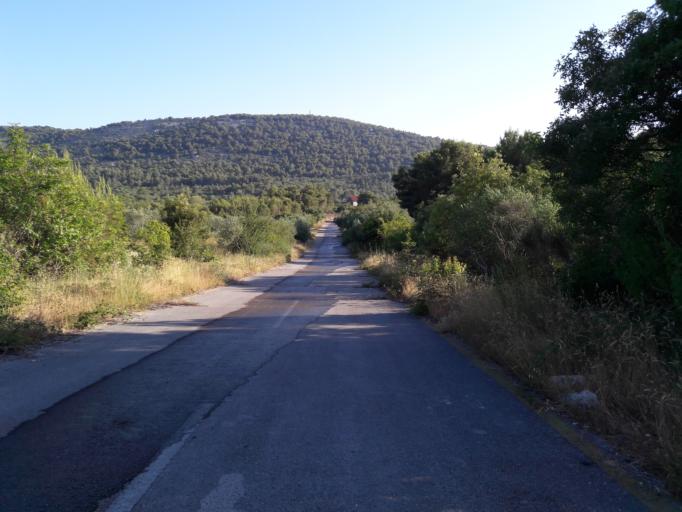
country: HR
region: Sibensko-Kniniska
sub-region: Grad Sibenik
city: Sibenik
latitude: 43.6971
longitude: 15.8470
